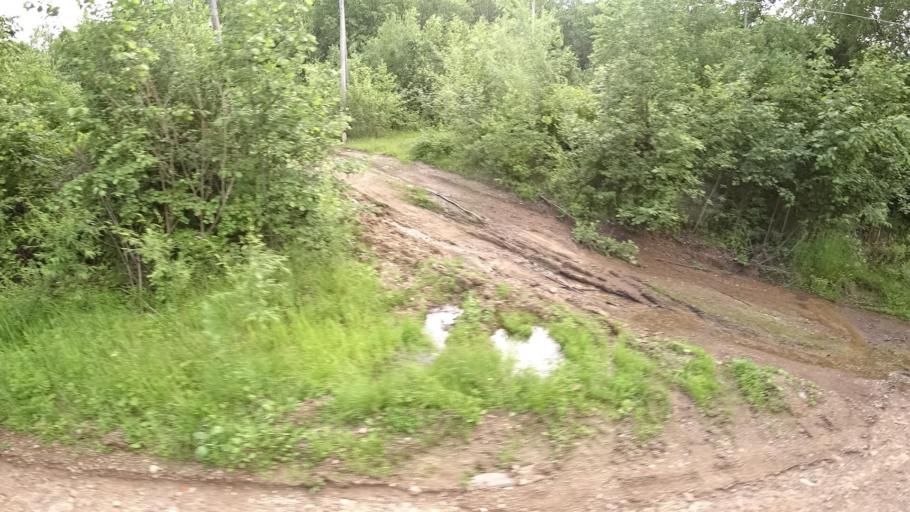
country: RU
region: Khabarovsk Krai
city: Litovko
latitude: 49.3622
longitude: 135.1792
